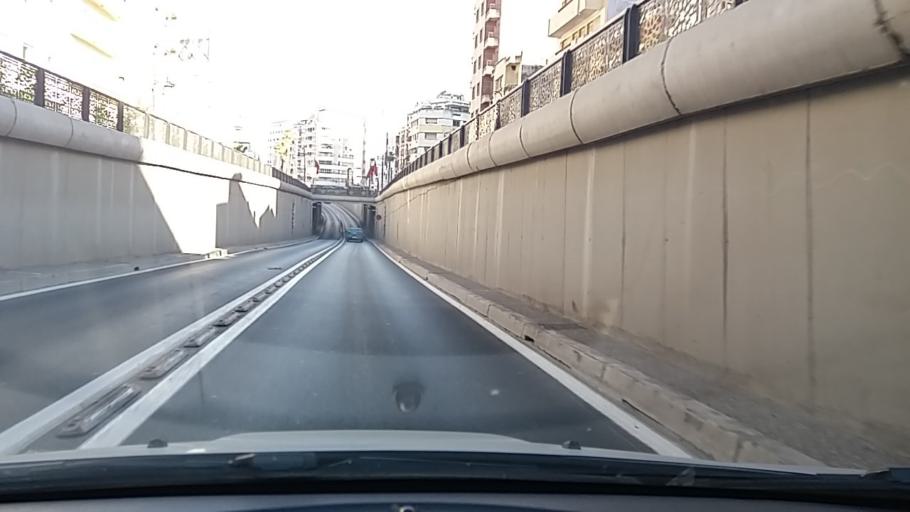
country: MA
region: Tanger-Tetouan
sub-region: Tanger-Assilah
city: Tangier
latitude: 35.7726
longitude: -5.8154
